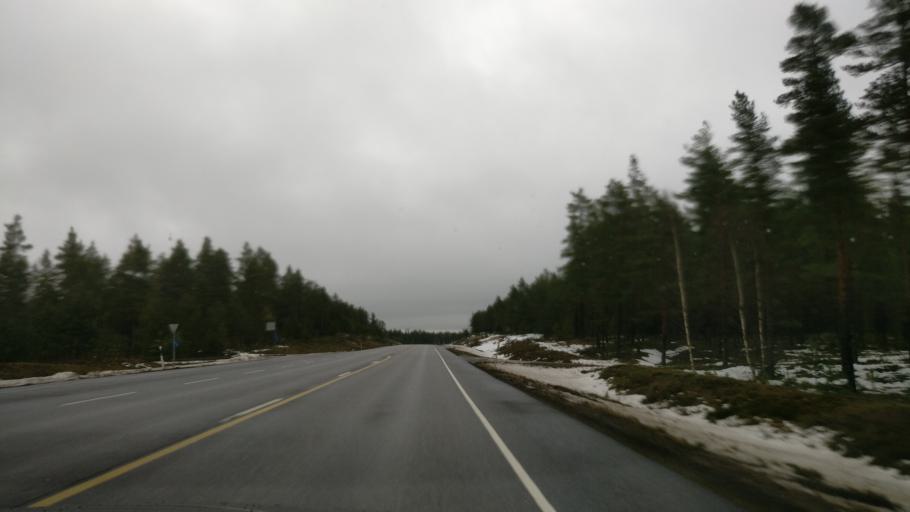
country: FI
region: Uusimaa
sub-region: Raaseporin
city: Hanko
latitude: 59.8951
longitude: 23.1839
